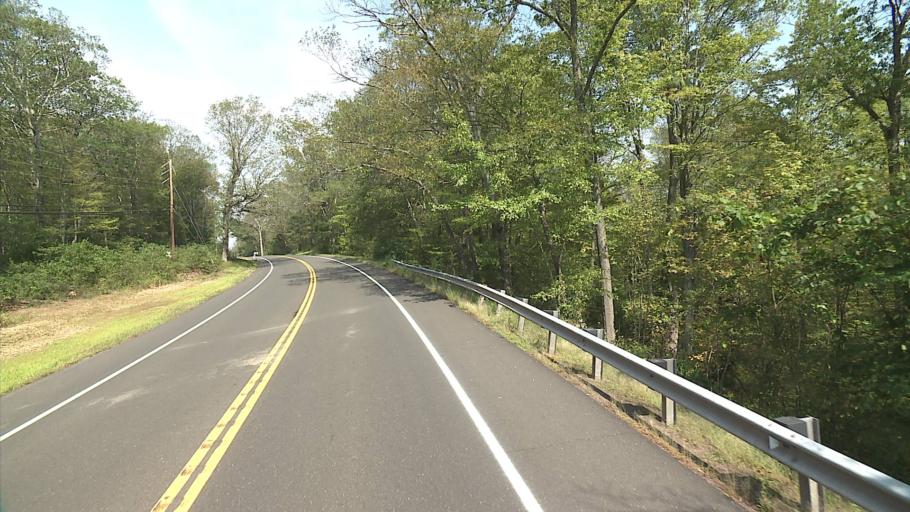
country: US
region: Connecticut
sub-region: New Haven County
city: Guilford
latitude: 41.3828
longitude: -72.6422
